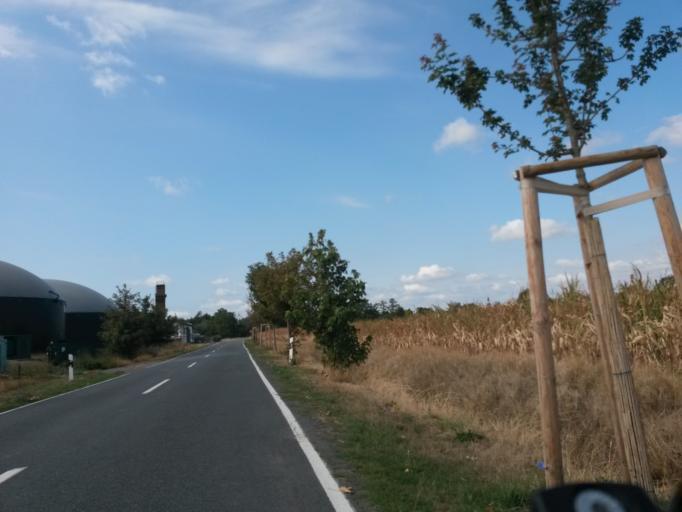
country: DE
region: Saxony-Anhalt
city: Elster
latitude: 51.8133
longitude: 12.7920
